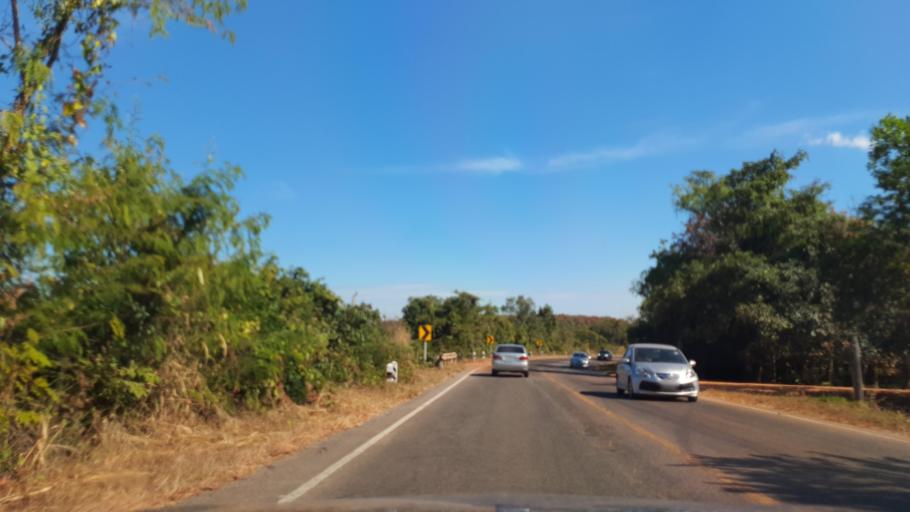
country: TH
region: Kalasin
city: Khao Wong
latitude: 16.7919
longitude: 104.1412
